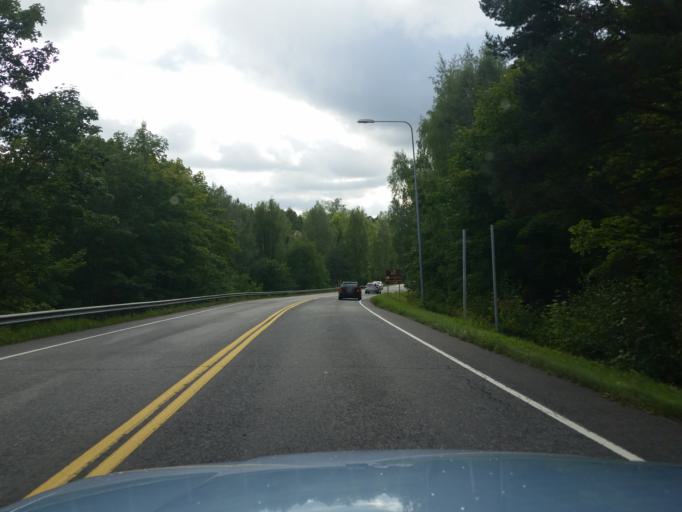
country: FI
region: Varsinais-Suomi
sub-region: Aboland-Turunmaa
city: Pargas
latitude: 60.3122
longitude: 22.3160
